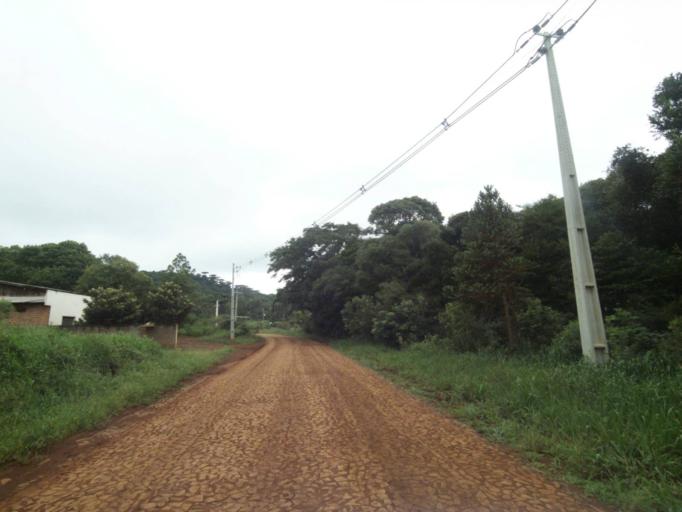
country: BR
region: Parana
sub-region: Pitanga
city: Pitanga
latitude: -24.9311
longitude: -51.8698
